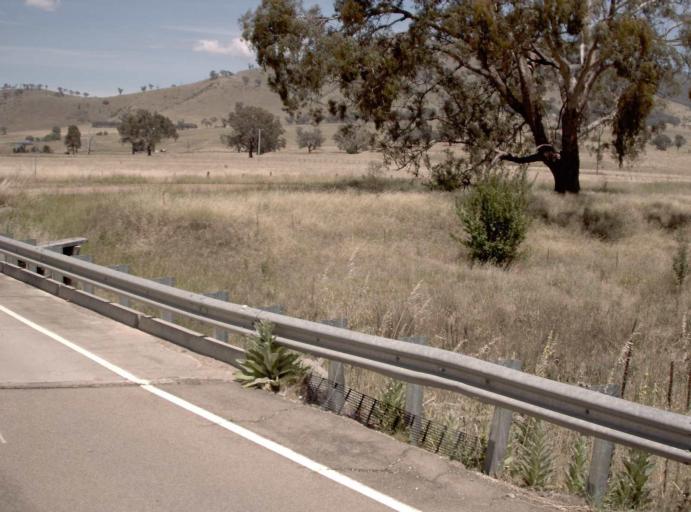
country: AU
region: Victoria
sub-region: East Gippsland
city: Bairnsdale
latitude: -37.2357
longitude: 147.7148
